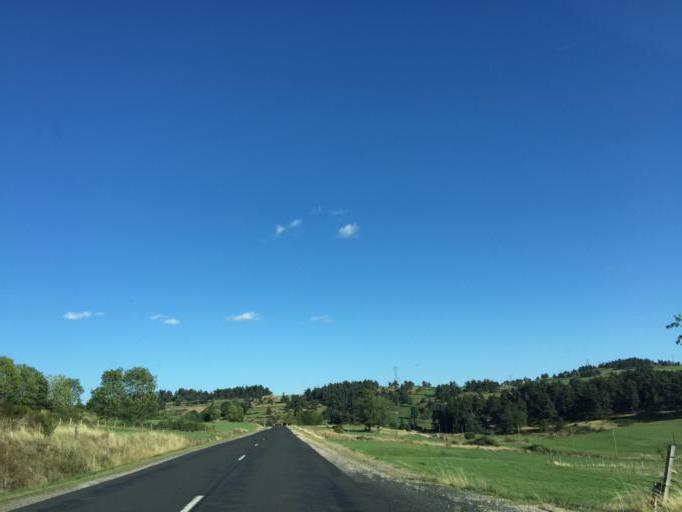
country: FR
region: Auvergne
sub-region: Departement de la Haute-Loire
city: Saugues
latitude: 44.9648
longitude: 3.5997
